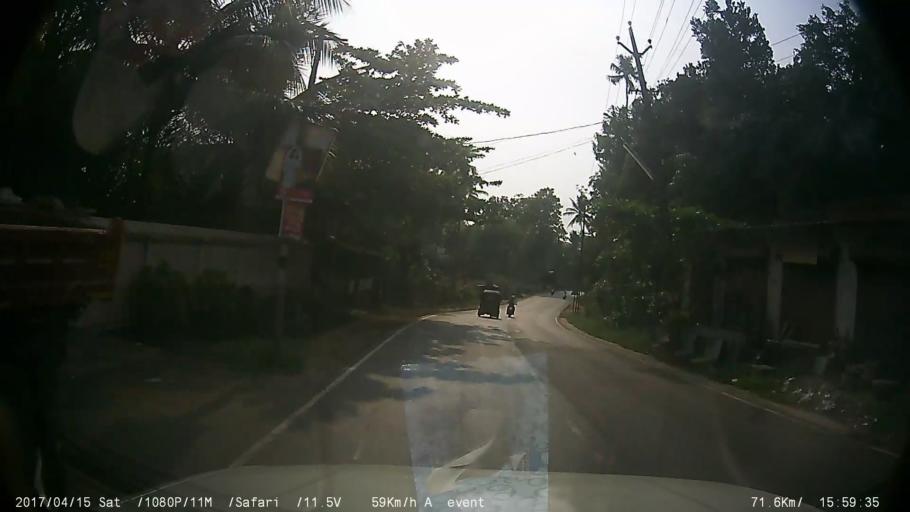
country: IN
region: Kerala
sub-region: Kottayam
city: Palackattumala
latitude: 9.6741
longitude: 76.5953
